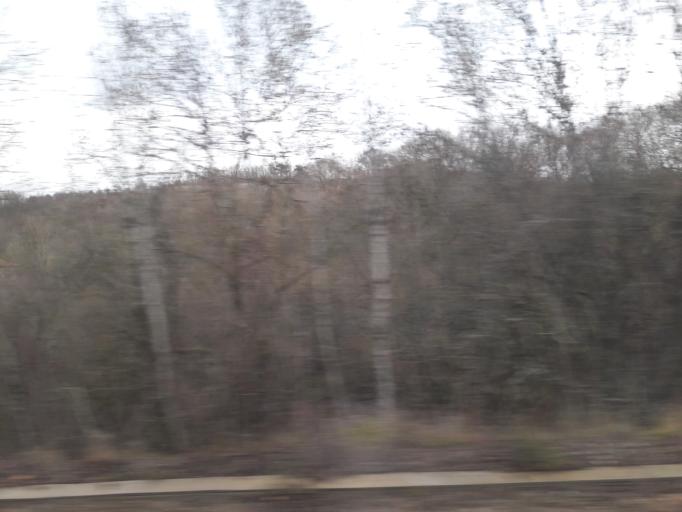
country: FR
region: Franche-Comte
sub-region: Territoire de Belfort
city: Danjoutin
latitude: 47.6213
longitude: 6.8650
